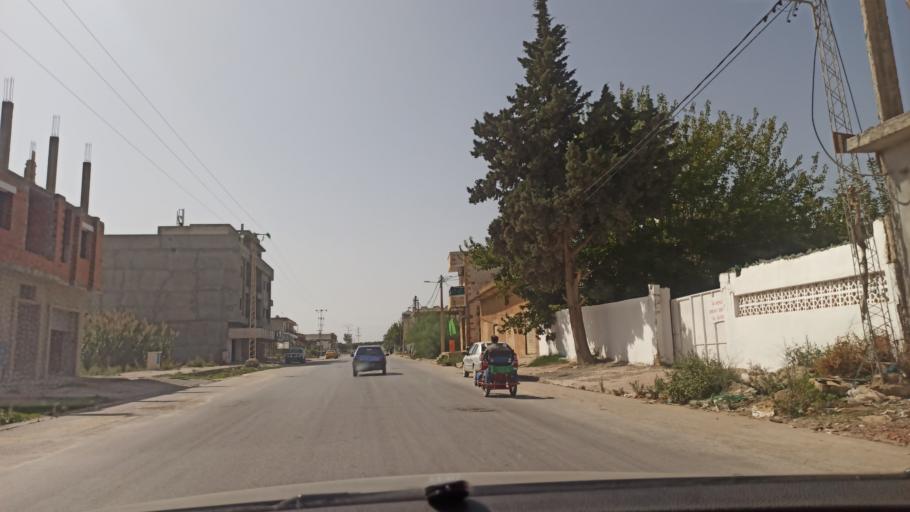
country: TN
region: Manouba
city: Manouba
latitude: 36.7543
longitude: 10.1019
